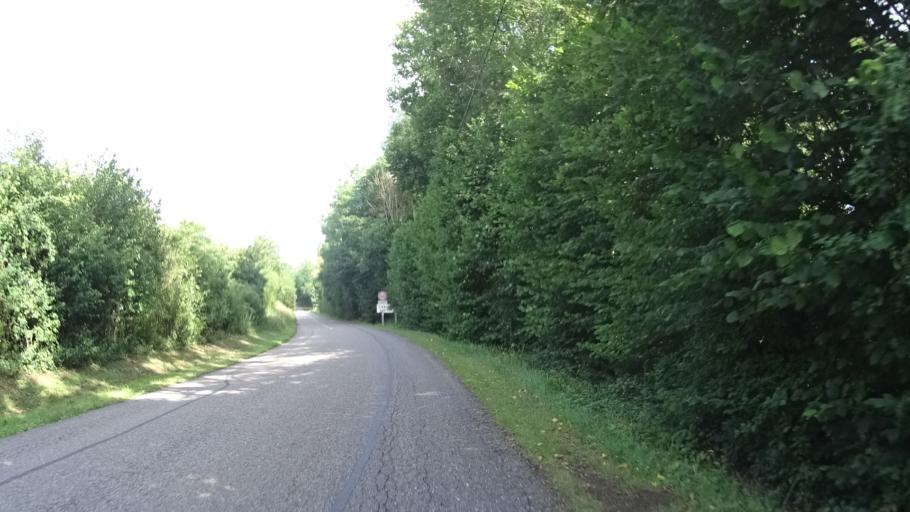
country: FR
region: Lorraine
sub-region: Departement de Meurthe-et-Moselle
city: Dommartin-les-Toul
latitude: 48.6491
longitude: 5.9103
